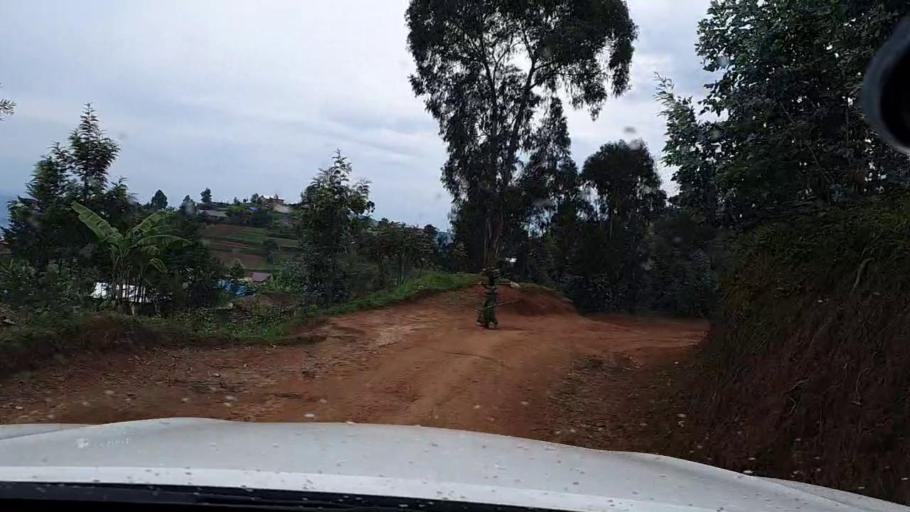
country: RW
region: Southern Province
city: Nzega
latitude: -2.3815
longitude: 29.2405
